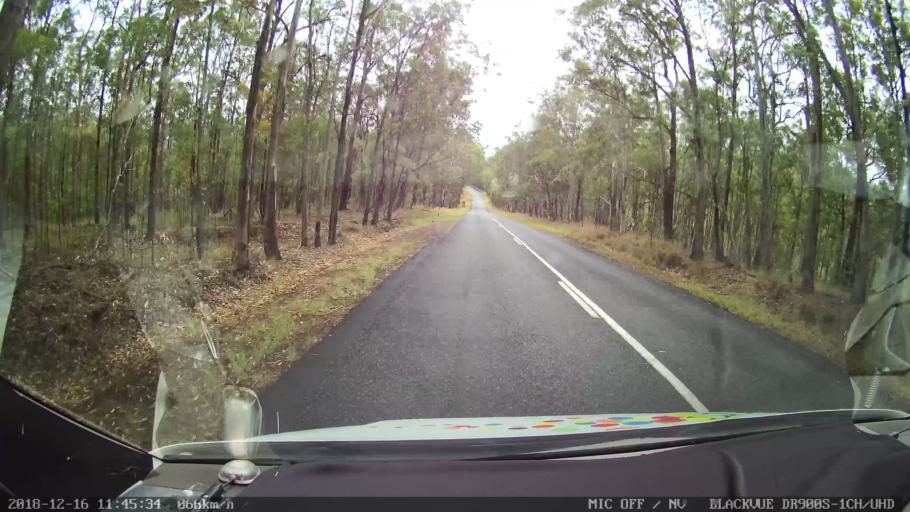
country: AU
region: New South Wales
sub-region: Tenterfield Municipality
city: Carrolls Creek
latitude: -28.9335
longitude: 152.2229
